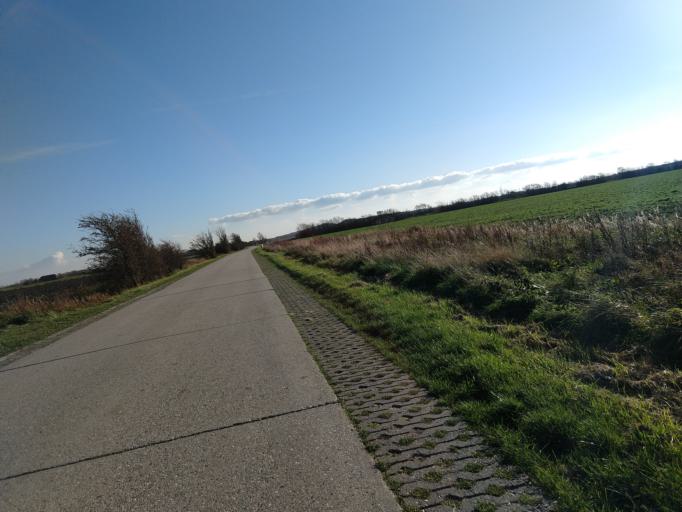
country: NL
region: Zeeland
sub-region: Gemeente Vlissingen
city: Vlissingen
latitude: 51.5202
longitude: 3.4861
